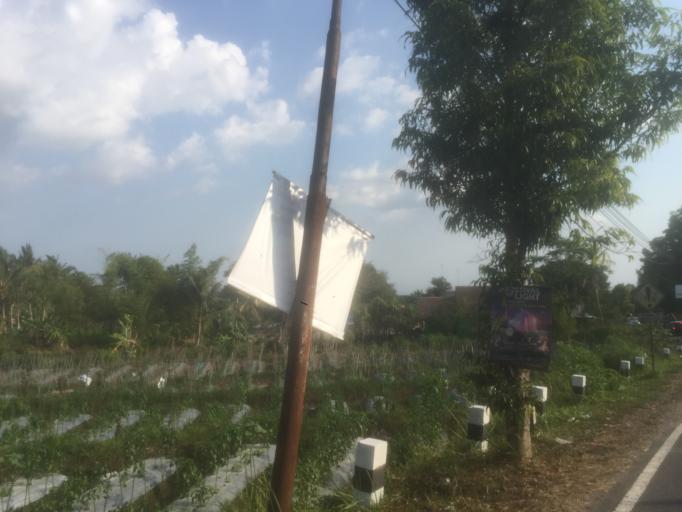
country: ID
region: Daerah Istimewa Yogyakarta
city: Sleman
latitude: -7.6564
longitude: 110.4231
